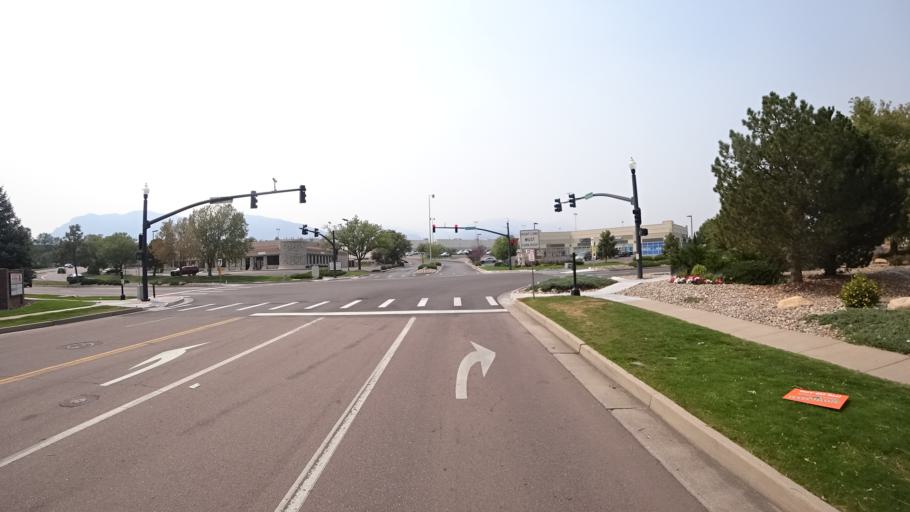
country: US
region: Colorado
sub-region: El Paso County
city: Stratmoor
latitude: 38.7925
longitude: -104.7991
